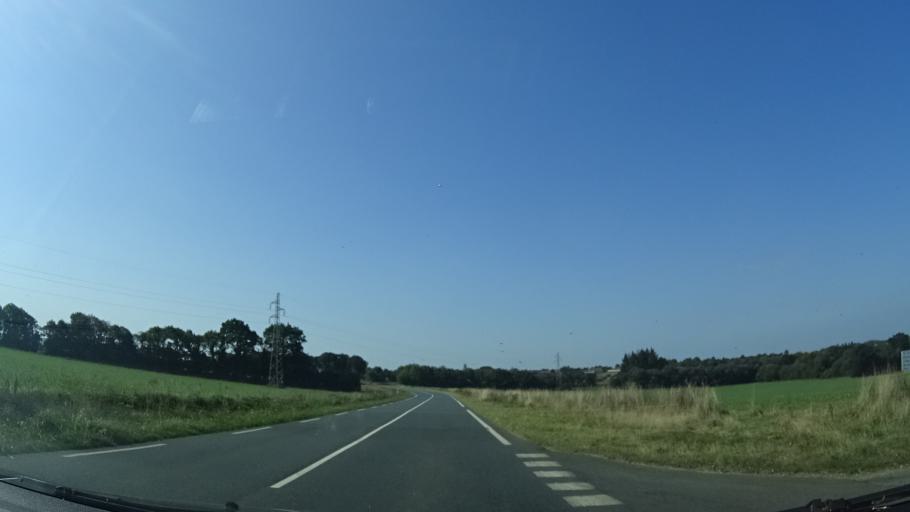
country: FR
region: Brittany
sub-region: Departement du Finistere
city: Cast
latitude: 48.1455
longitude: -4.1566
